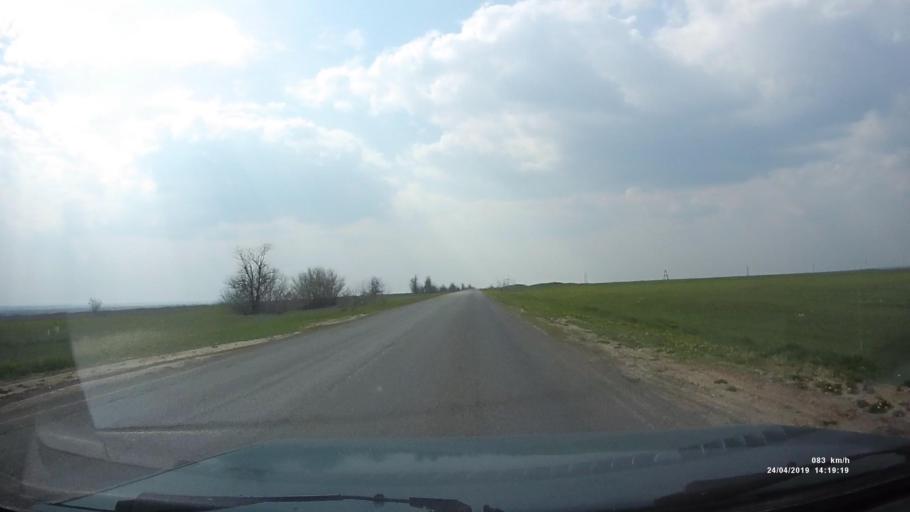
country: RU
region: Kalmykiya
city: Arshan'
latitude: 46.3050
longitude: 44.1779
